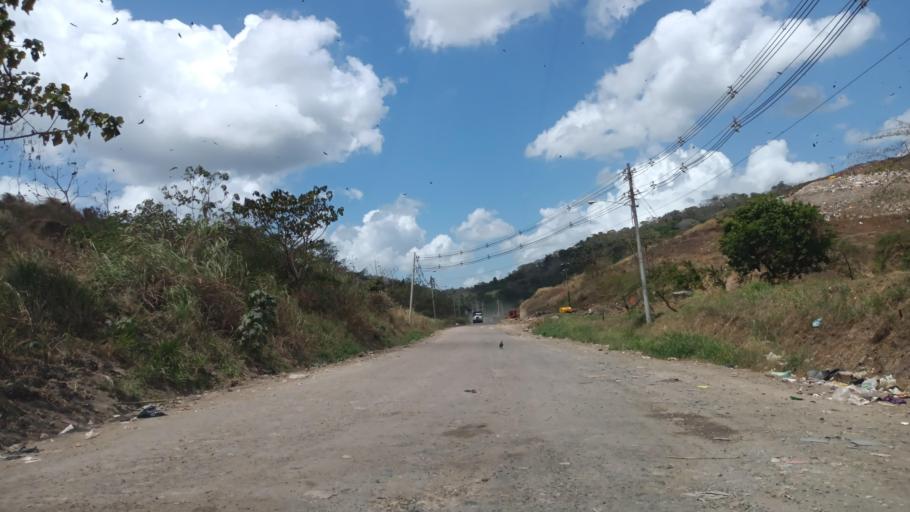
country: PA
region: Panama
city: Las Cumbres
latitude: 9.0534
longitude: -79.5637
